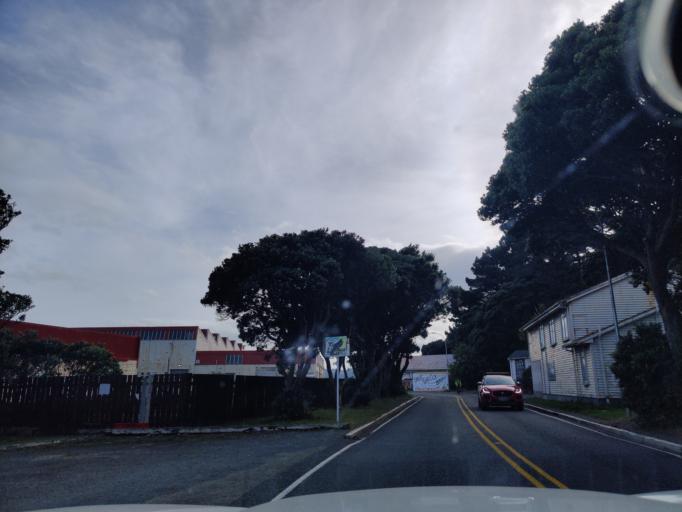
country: NZ
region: Wellington
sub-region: Wellington City
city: Wellington
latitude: -41.2951
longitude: 174.8221
